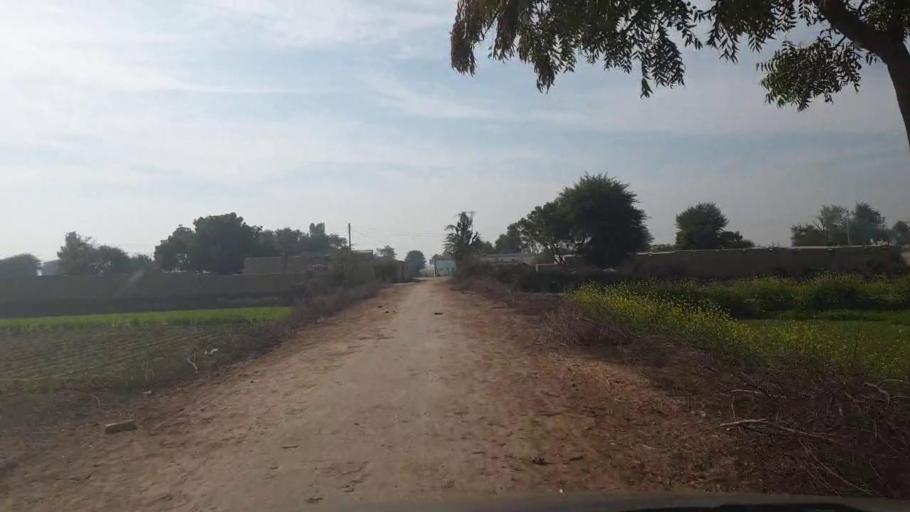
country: PK
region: Sindh
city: Shahpur Chakar
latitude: 26.1826
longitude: 68.5928
